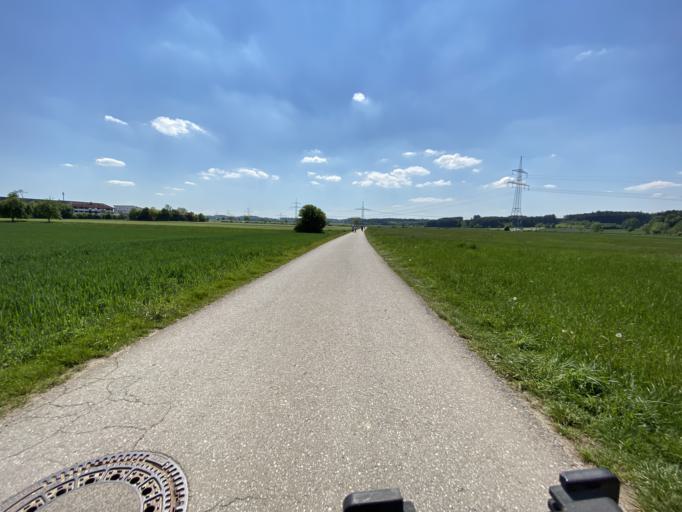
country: DE
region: Bavaria
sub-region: Upper Bavaria
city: Puchheim
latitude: 48.1329
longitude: 11.3488
